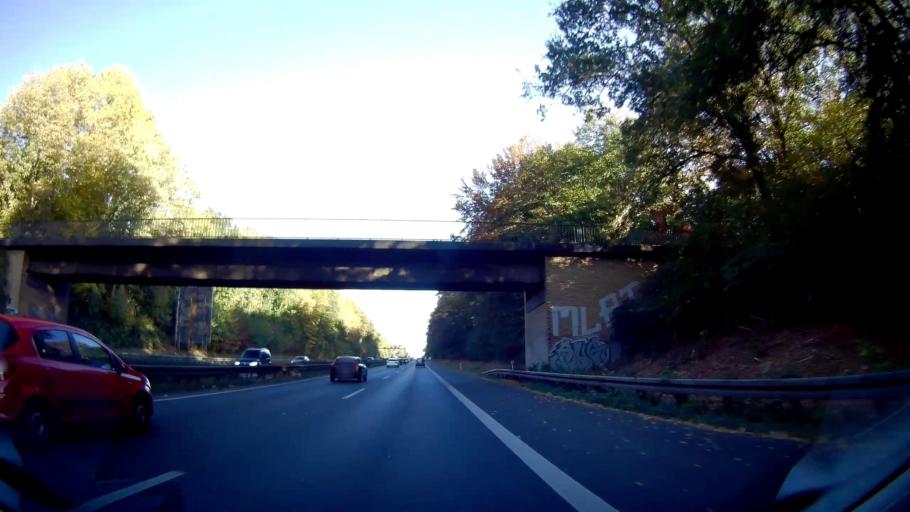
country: DE
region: North Rhine-Westphalia
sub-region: Regierungsbezirk Arnsberg
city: Herne
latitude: 51.5115
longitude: 7.2239
